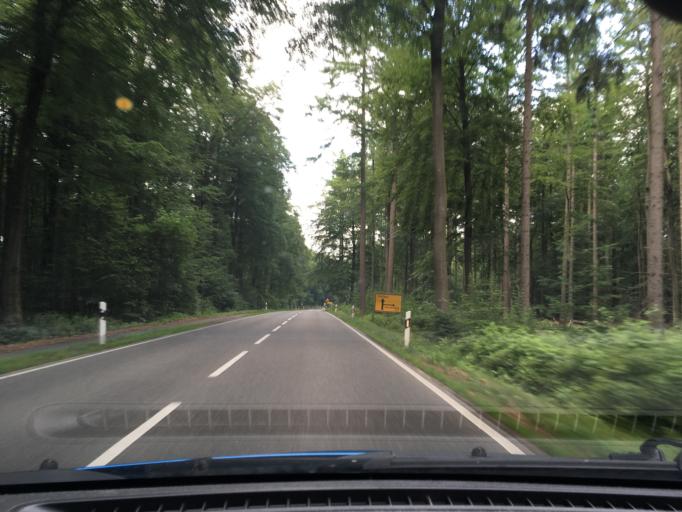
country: DE
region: Lower Saxony
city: Bendestorf
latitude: 53.3414
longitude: 9.9429
